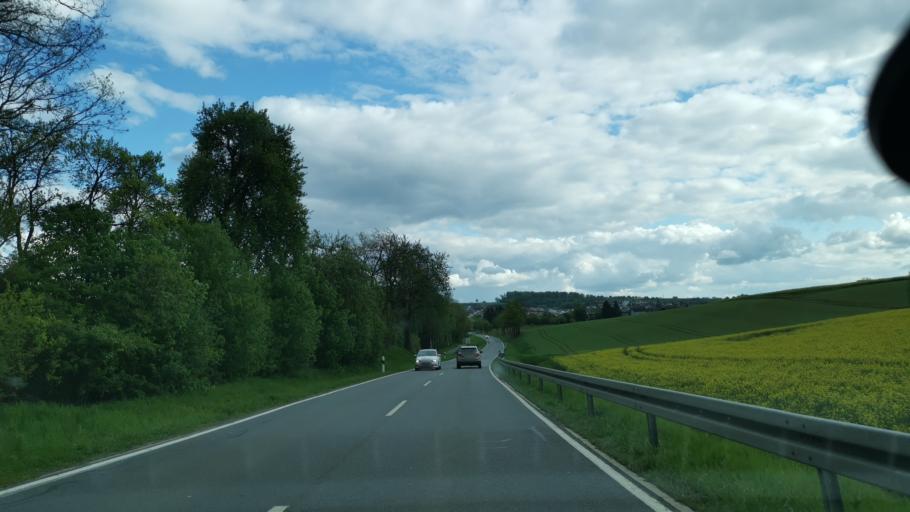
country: DE
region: Baden-Wuerttemberg
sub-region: Karlsruhe Region
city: Osterburken
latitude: 49.4430
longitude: 9.4278
